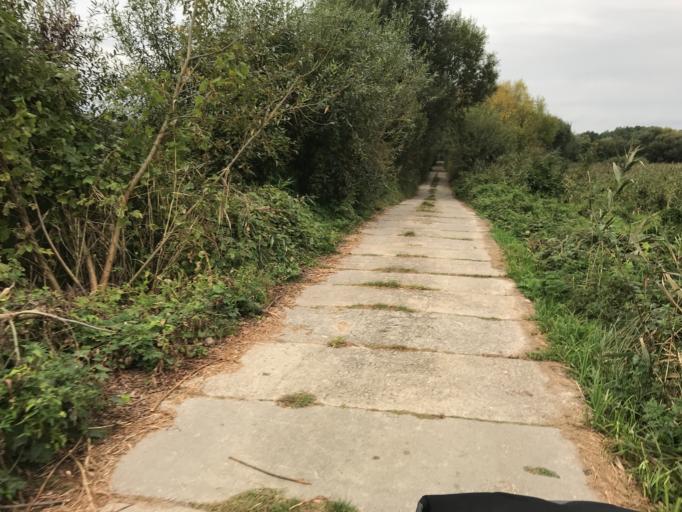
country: PL
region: Podlasie
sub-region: Powiat bialostocki
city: Tykocin
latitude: 53.1392
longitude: 22.8711
